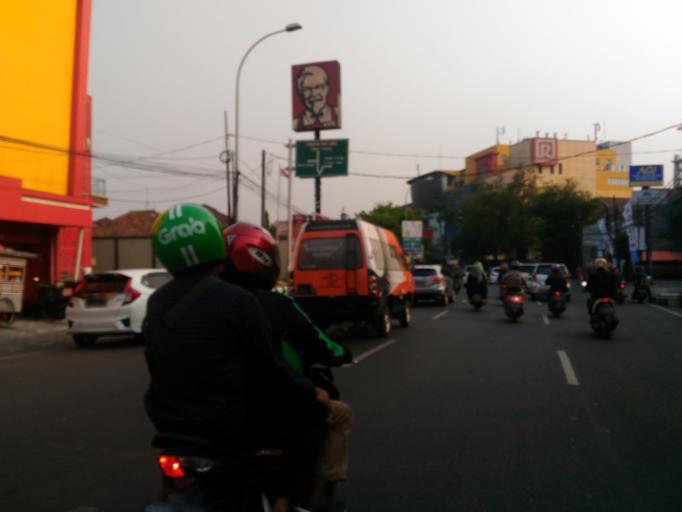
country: ID
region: Banten
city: Tangerang
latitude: -6.1732
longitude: 106.6306
